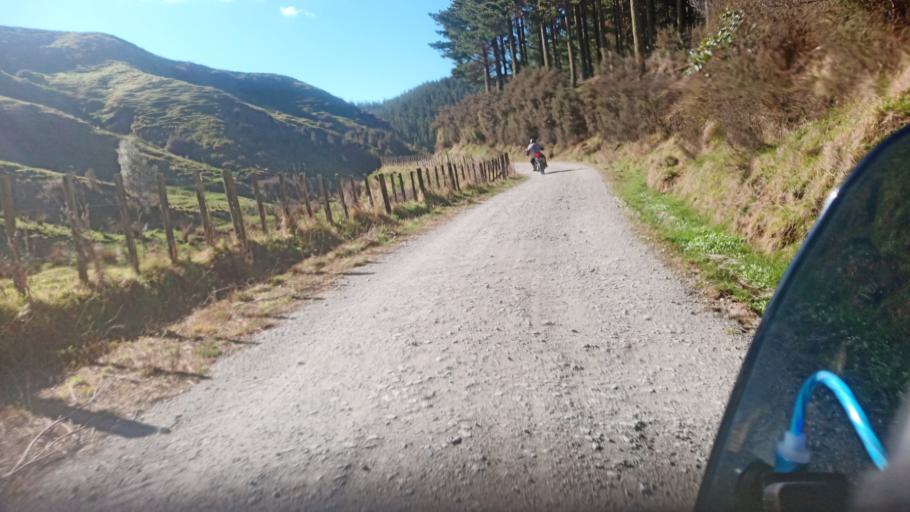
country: NZ
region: Hawke's Bay
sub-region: Wairoa District
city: Wairoa
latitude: -38.6594
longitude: 177.4890
